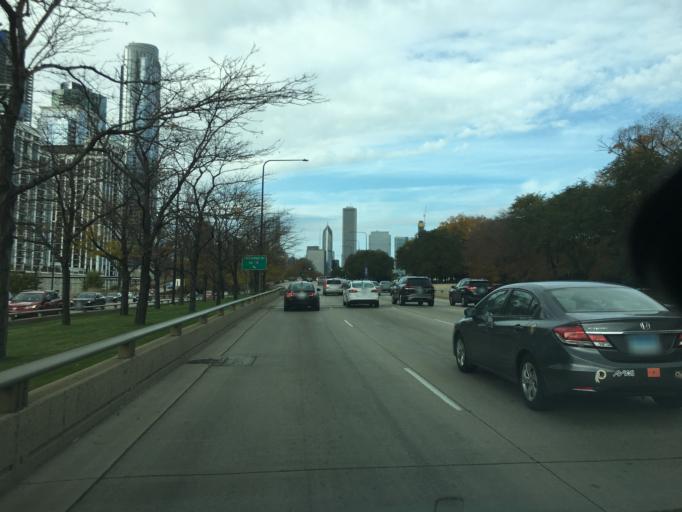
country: US
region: Illinois
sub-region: Cook County
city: Chicago
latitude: 41.8628
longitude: -87.6186
